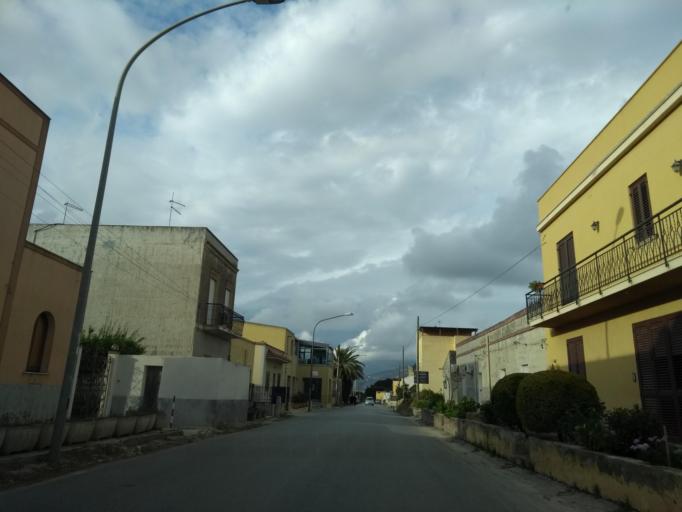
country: IT
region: Sicily
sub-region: Trapani
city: Marausa
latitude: 37.9516
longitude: 12.5146
